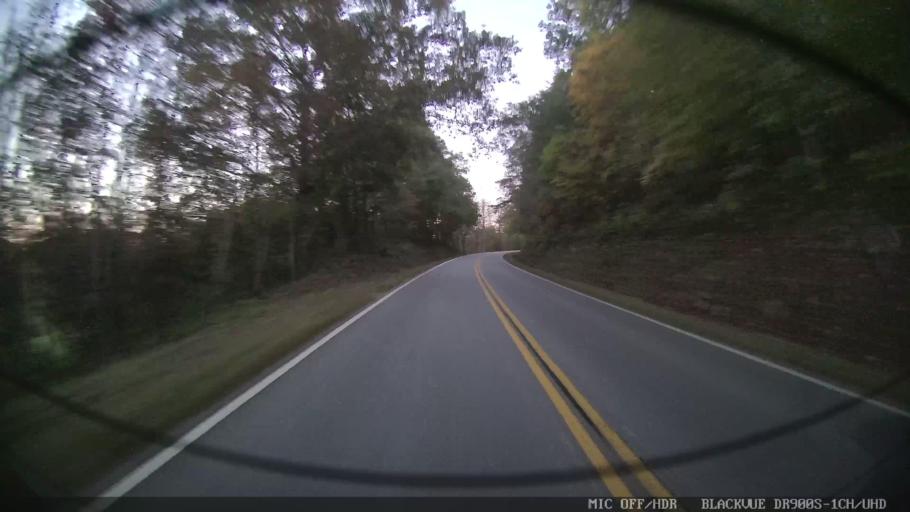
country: US
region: North Carolina
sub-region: Clay County
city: Hayesville
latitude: 34.9538
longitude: -83.8614
